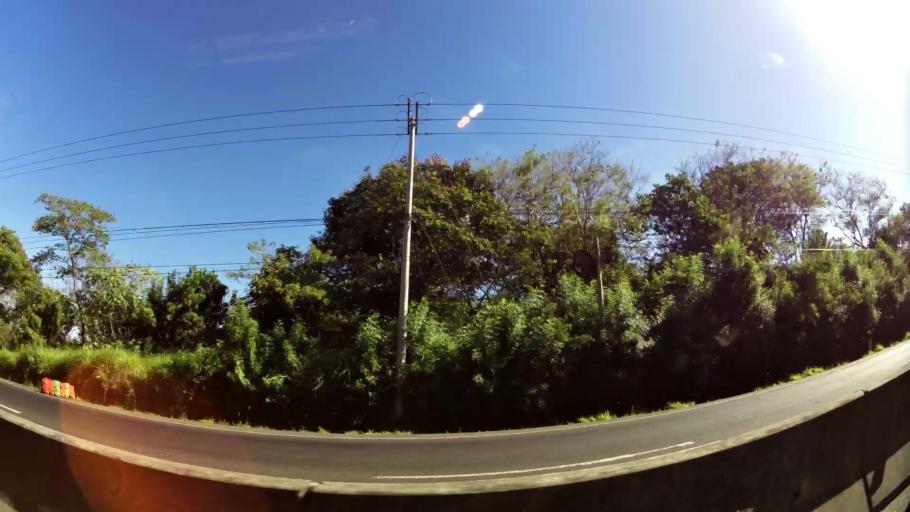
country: SV
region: Santa Ana
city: Santa Ana
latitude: 13.9522
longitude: -89.5595
